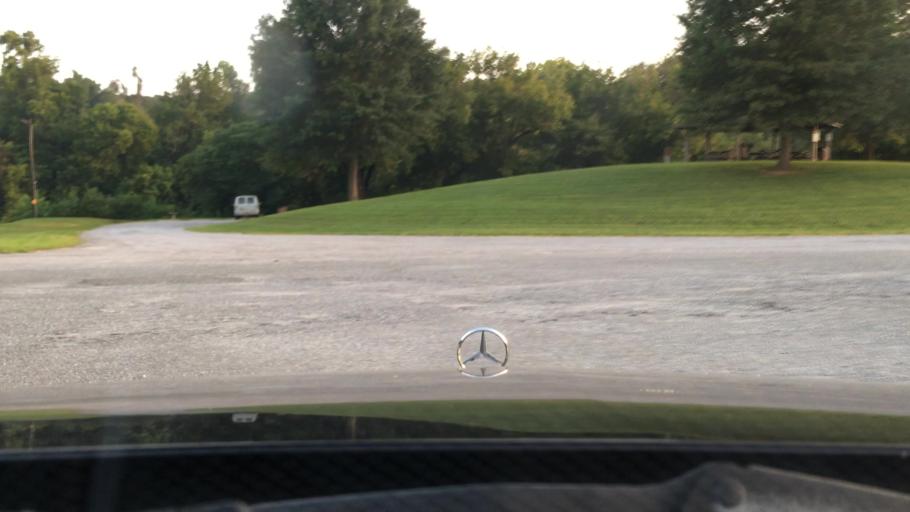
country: US
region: Virginia
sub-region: Campbell County
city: Altavista
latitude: 37.1066
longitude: -79.2866
